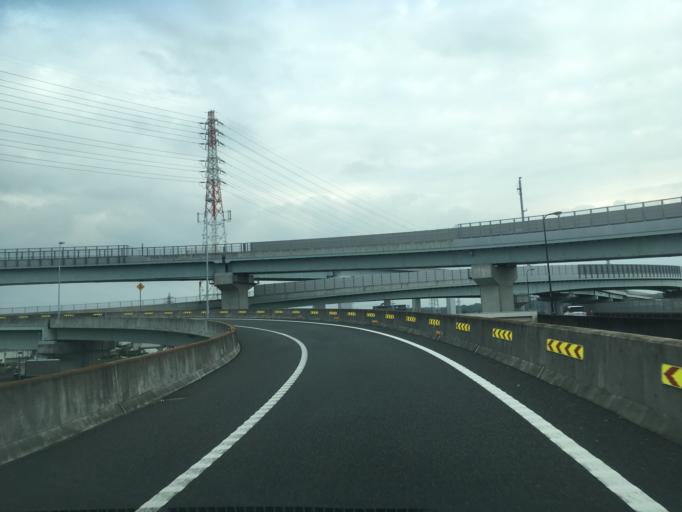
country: JP
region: Kanagawa
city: Chigasaki
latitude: 35.3496
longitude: 139.3918
